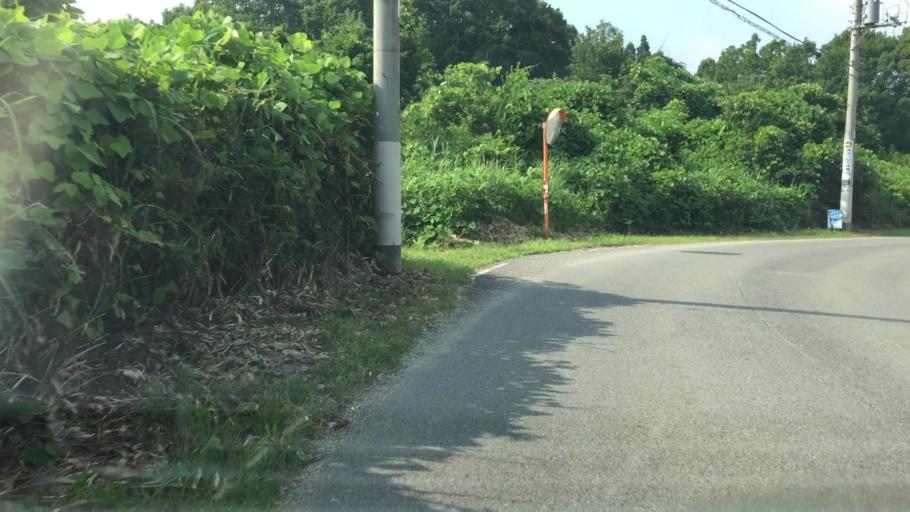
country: JP
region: Tochigi
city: Kuroiso
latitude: 37.0423
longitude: 140.0270
